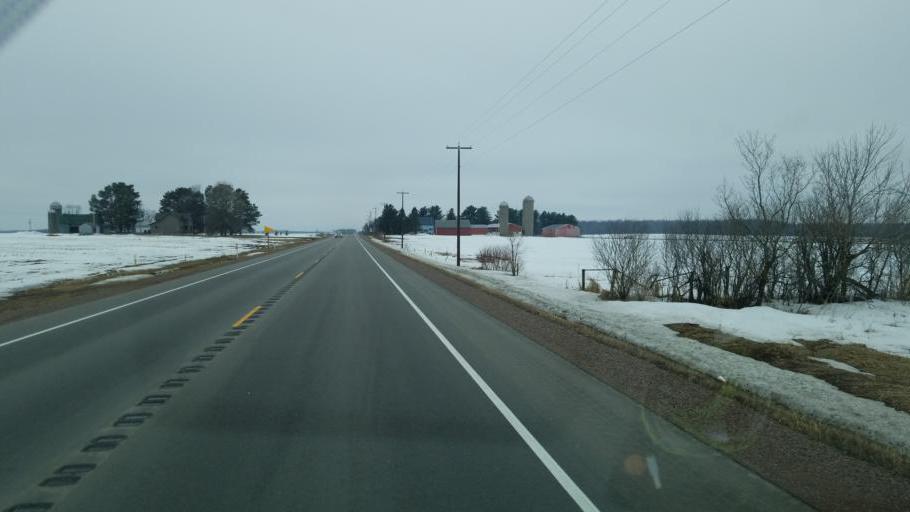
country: US
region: Wisconsin
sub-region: Marathon County
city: Spencer
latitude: 44.6563
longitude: -90.2941
